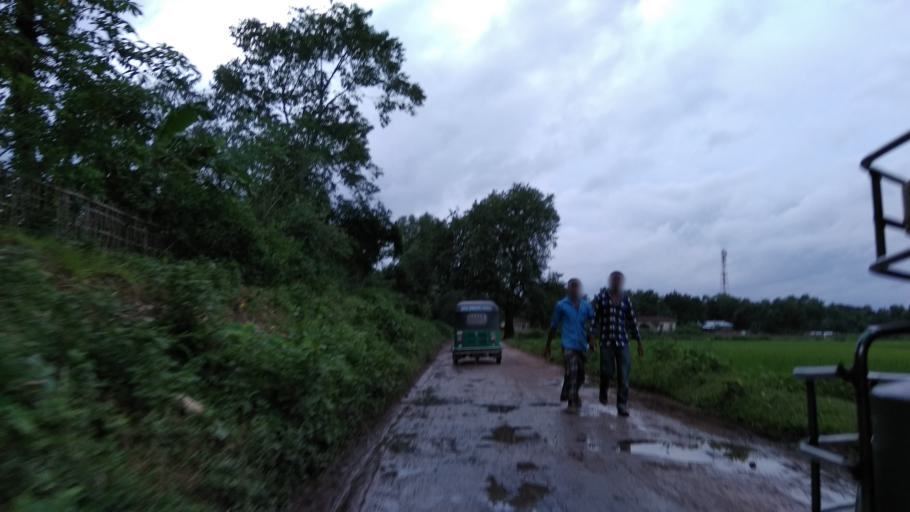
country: IN
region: Tripura
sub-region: Dhalai
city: Kamalpur
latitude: 24.2120
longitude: 91.8585
